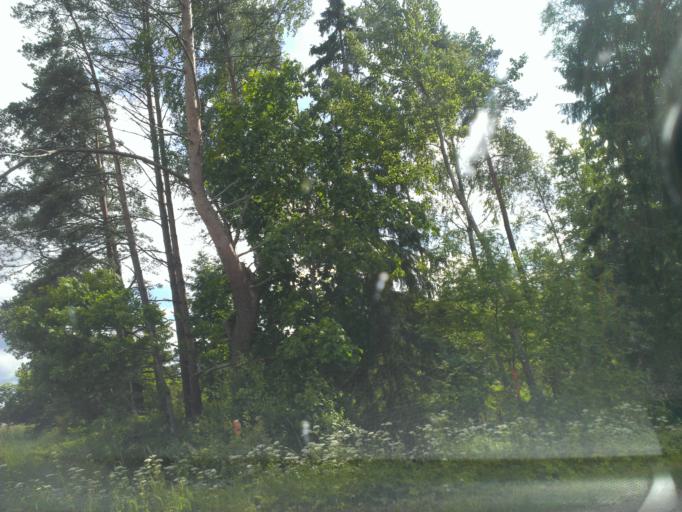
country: LV
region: Grobina
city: Grobina
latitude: 56.4041
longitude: 21.2379
